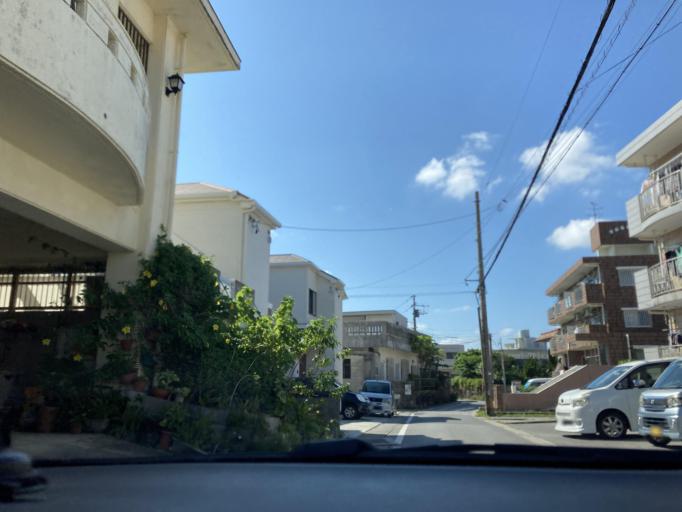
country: JP
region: Okinawa
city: Ginowan
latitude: 26.2241
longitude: 127.7314
